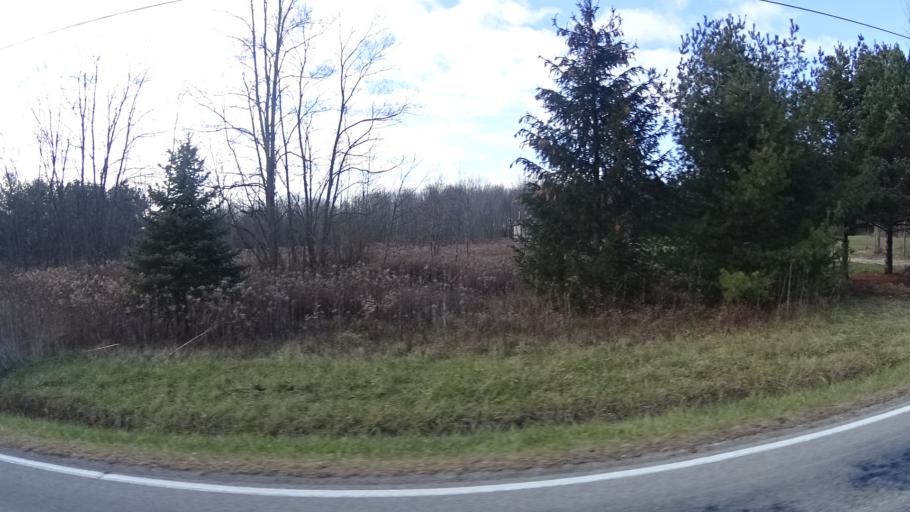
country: US
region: Ohio
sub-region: Lorain County
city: Wellington
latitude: 41.1630
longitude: -82.2689
